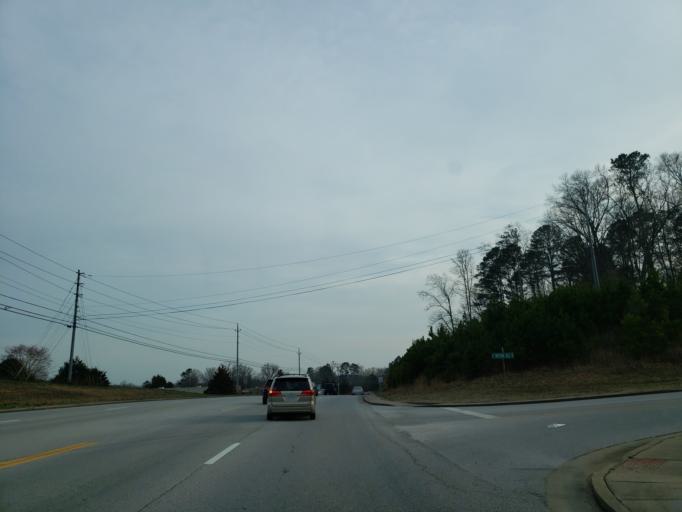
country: US
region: Tennessee
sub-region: Bradley County
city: Wildwood Lake
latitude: 35.1106
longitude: -84.8626
